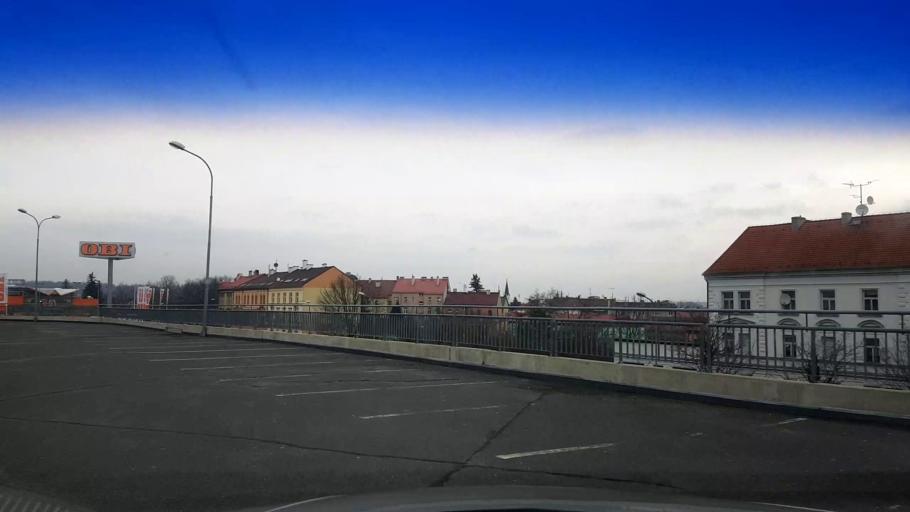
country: CZ
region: Karlovarsky
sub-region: Okres Cheb
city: Cheb
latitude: 50.0715
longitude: 12.3701
